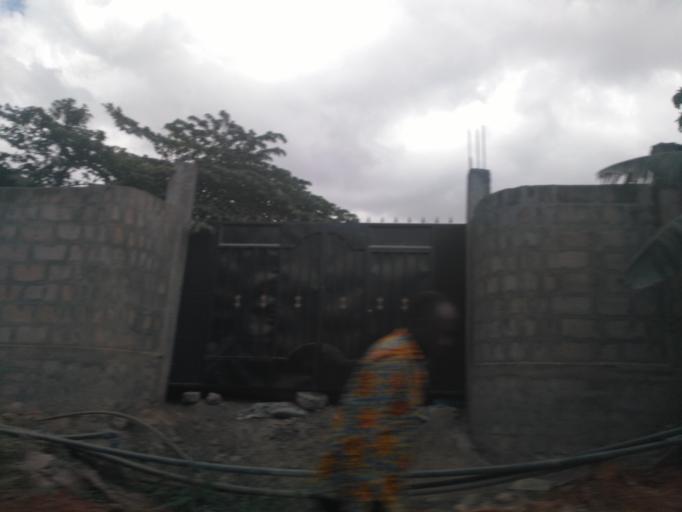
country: TZ
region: Dar es Salaam
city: Dar es Salaam
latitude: -6.8911
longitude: 39.2857
